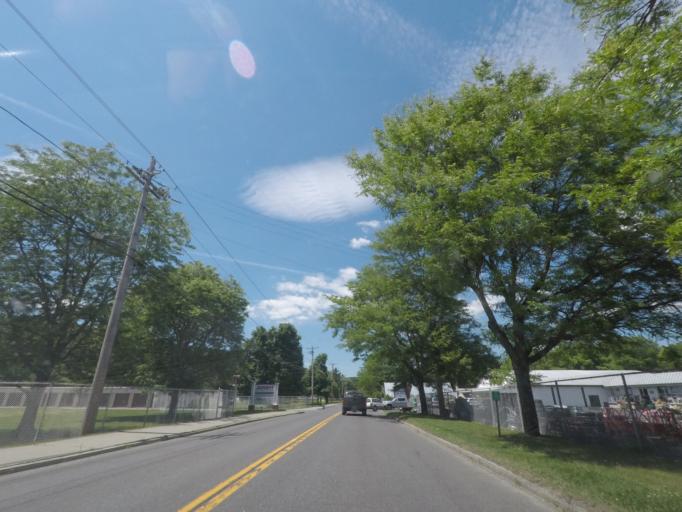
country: US
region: New York
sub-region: Dutchess County
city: Pine Plains
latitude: 41.9564
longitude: -73.5156
